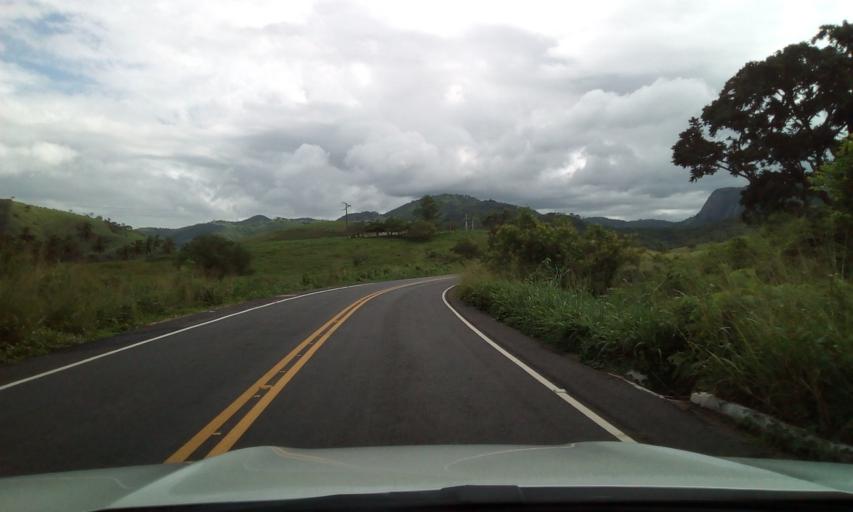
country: BR
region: Paraiba
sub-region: Alagoinha
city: Alagoinha
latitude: -6.8928
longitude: -35.5578
